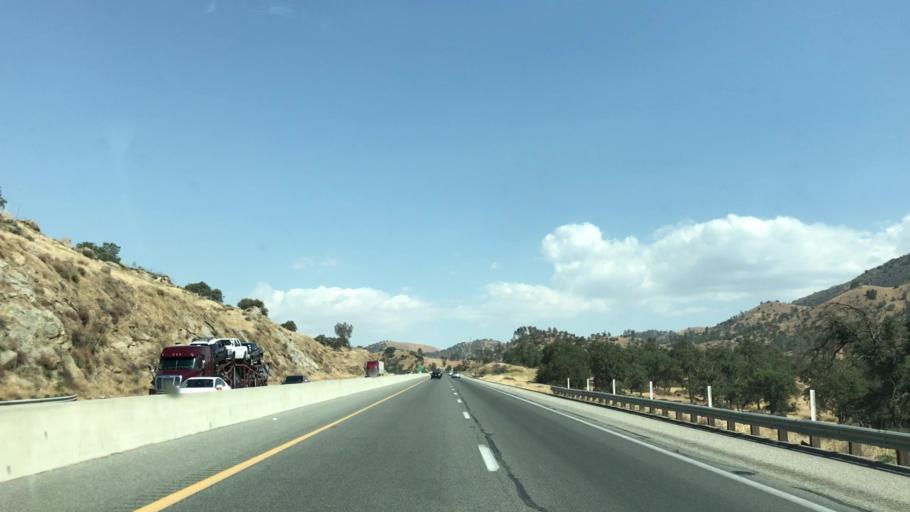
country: US
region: California
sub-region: Kern County
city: Golden Hills
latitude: 35.2065
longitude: -118.5339
